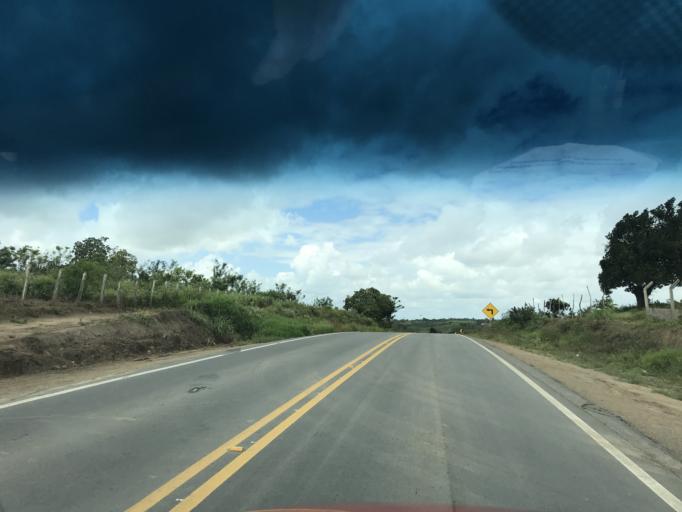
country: BR
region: Bahia
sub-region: Conceicao Do Almeida
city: Conceicao do Almeida
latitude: -12.7018
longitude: -39.2361
